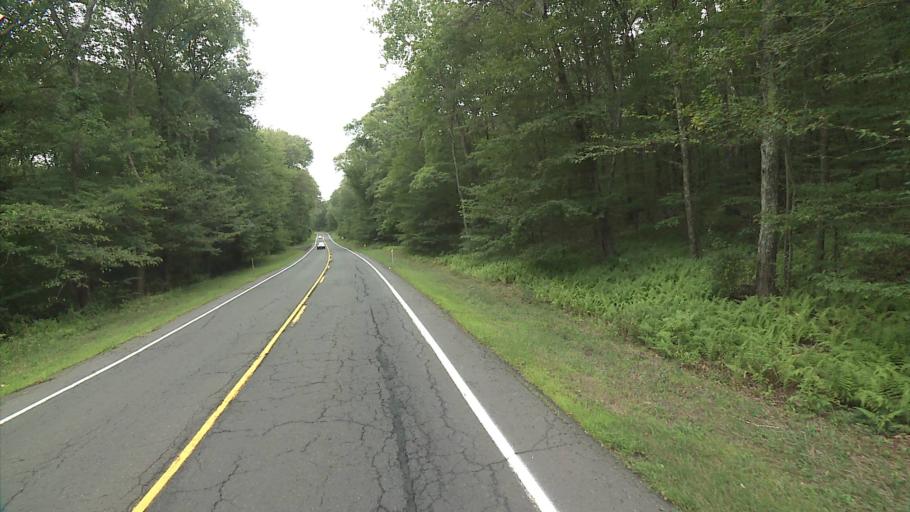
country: US
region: Connecticut
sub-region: Hartford County
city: Manchester
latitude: 41.7678
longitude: -72.4621
